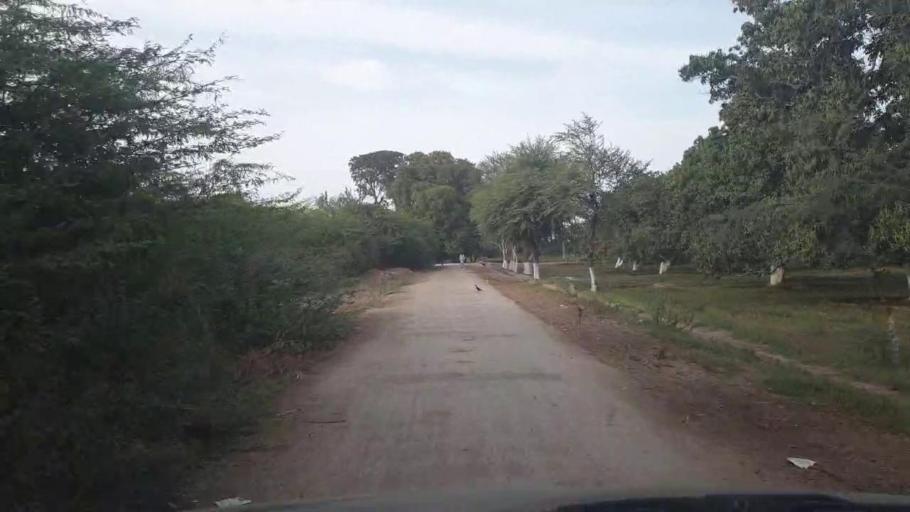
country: PK
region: Sindh
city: Kunri
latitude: 25.2707
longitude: 69.5585
